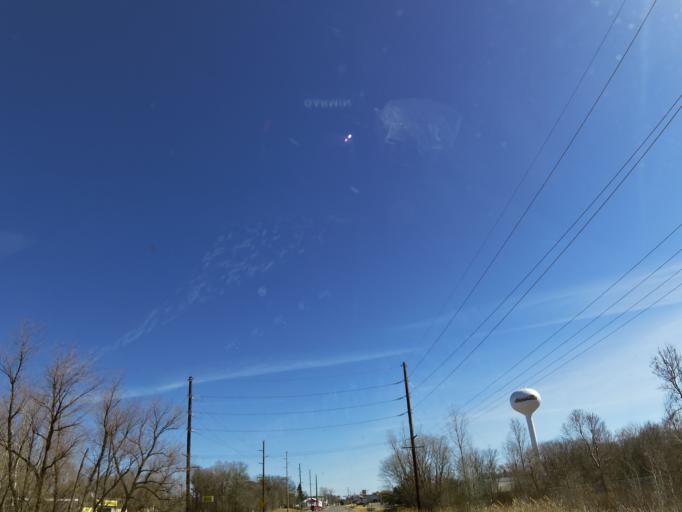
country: US
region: Minnesota
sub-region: Wright County
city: Annandale
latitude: 45.2641
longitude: -94.1318
